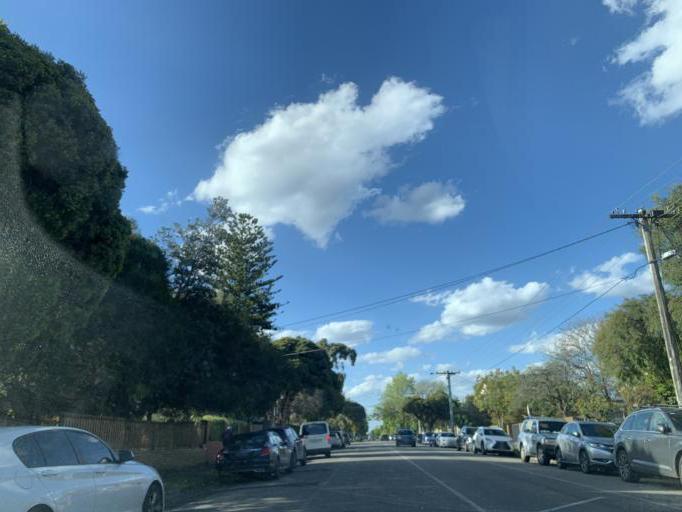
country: AU
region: Victoria
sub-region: Bayside
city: North Brighton
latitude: -37.9047
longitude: 145.0017
